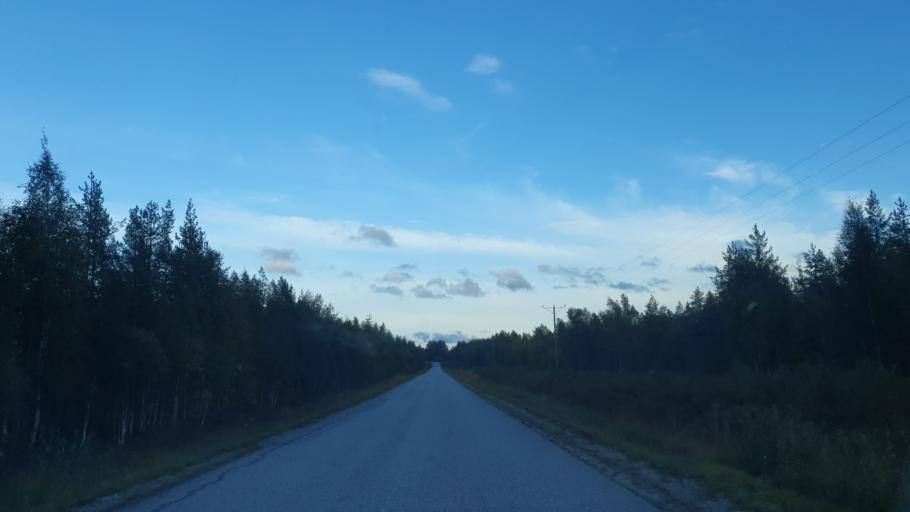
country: FI
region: Kainuu
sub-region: Kehys-Kainuu
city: Kuhmo
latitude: 64.4171
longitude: 29.9326
